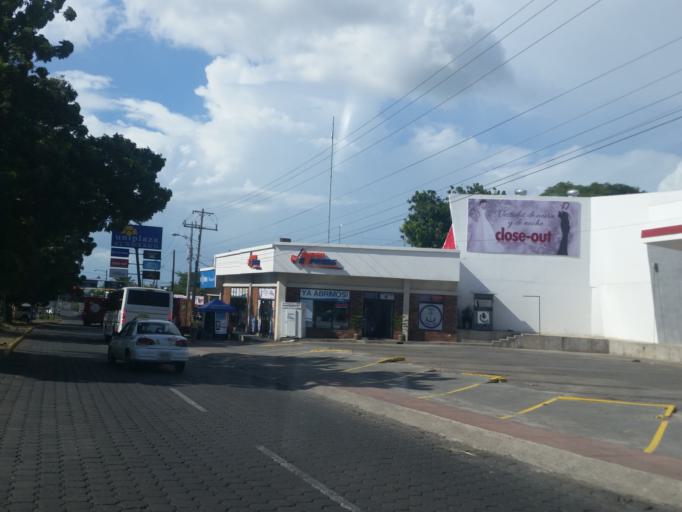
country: NI
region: Managua
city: Managua
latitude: 12.1359
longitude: -86.2505
